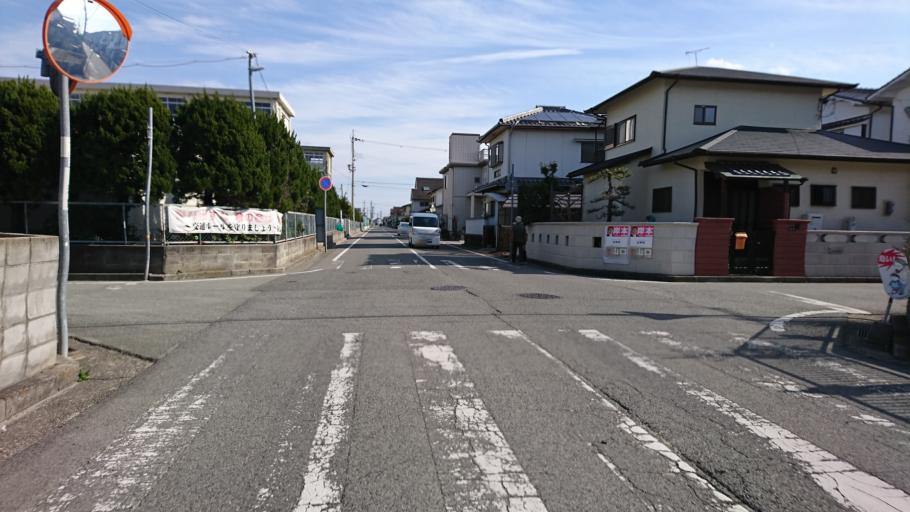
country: JP
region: Hyogo
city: Kakogawacho-honmachi
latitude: 34.7902
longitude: 134.8248
